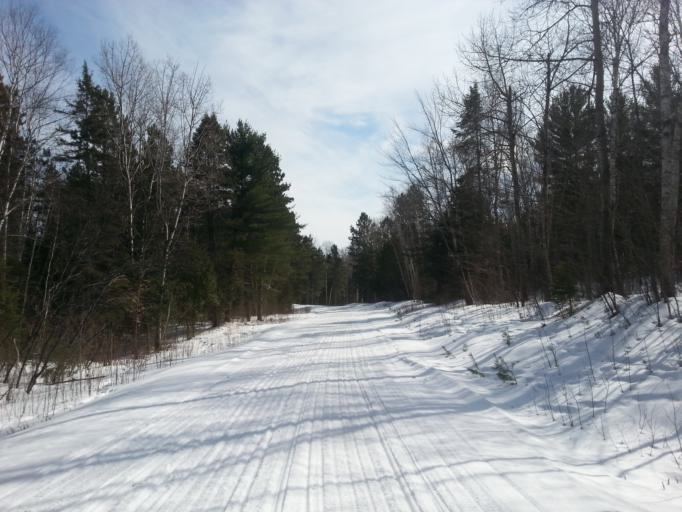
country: CA
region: Ontario
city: Greater Sudbury
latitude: 46.3408
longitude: -80.9024
